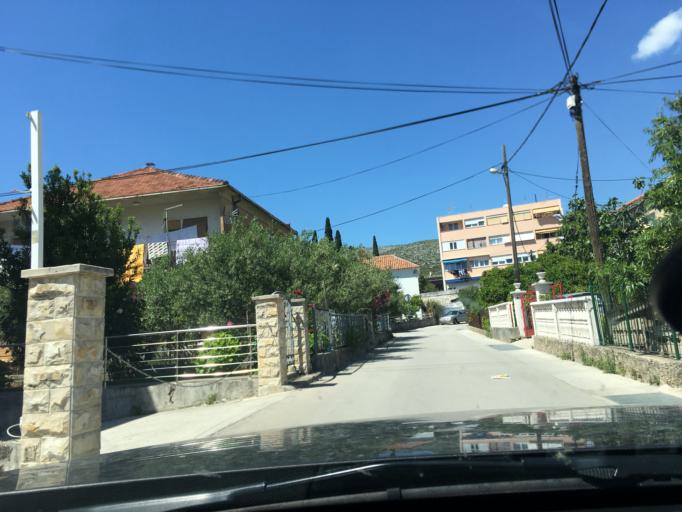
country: HR
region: Splitsko-Dalmatinska
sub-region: Grad Trogir
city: Trogir
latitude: 43.5193
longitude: 16.2540
